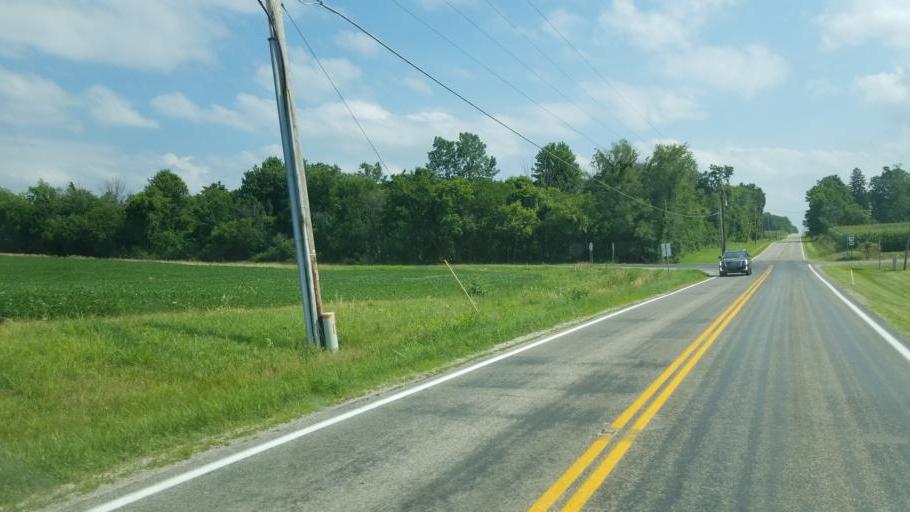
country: US
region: Ohio
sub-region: Crawford County
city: Crestline
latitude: 40.8874
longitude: -82.7724
